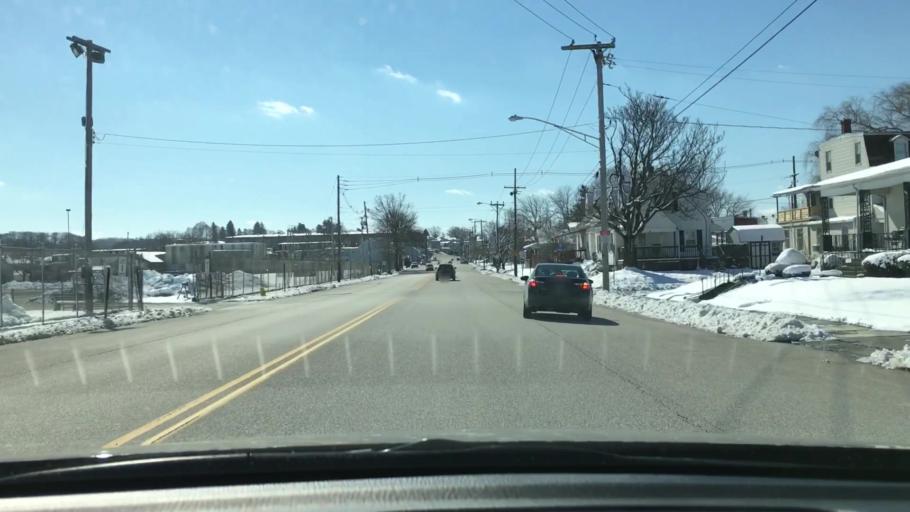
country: US
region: Pennsylvania
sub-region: York County
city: West York
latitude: 39.9581
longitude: -76.7597
